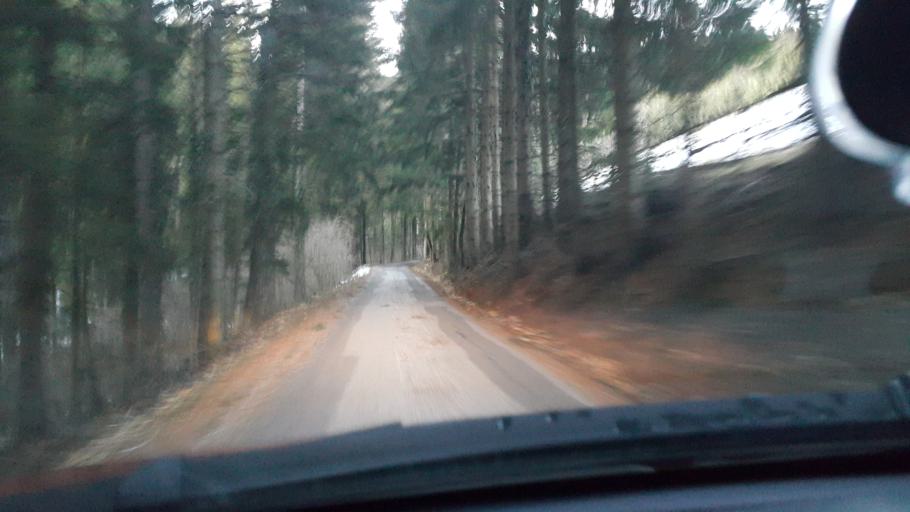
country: AT
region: Styria
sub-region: Politischer Bezirk Graz-Umgebung
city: Stiwoll
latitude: 47.1303
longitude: 15.2213
